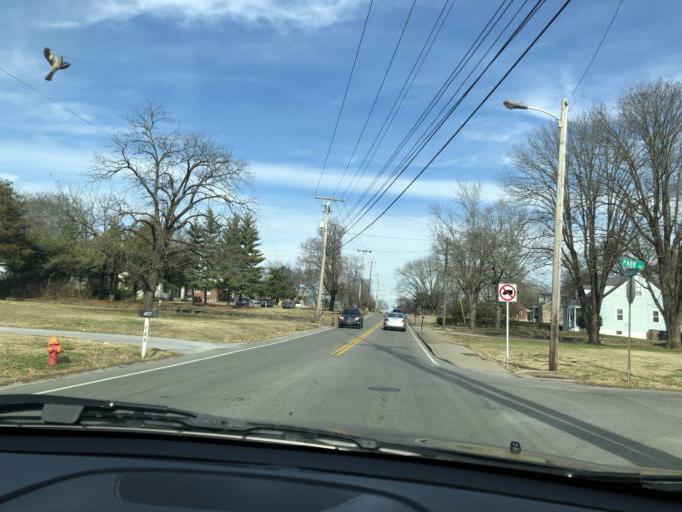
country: US
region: Tennessee
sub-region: Davidson County
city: Lakewood
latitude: 36.1714
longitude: -86.6795
